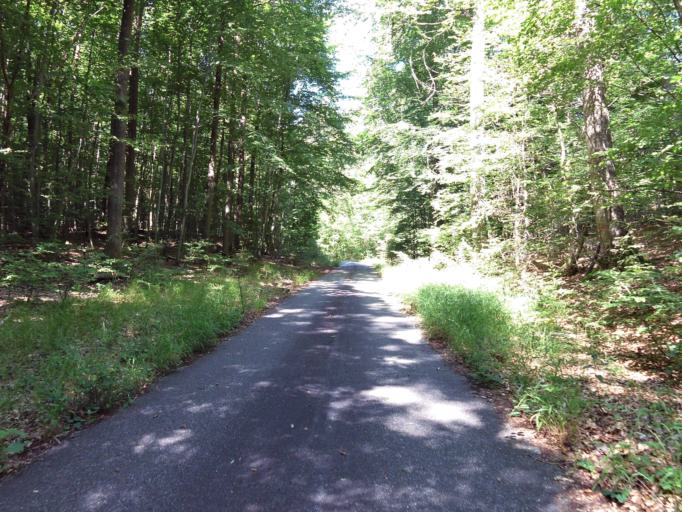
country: DE
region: Rheinland-Pfalz
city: Elmstein
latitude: 49.3816
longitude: 7.9480
